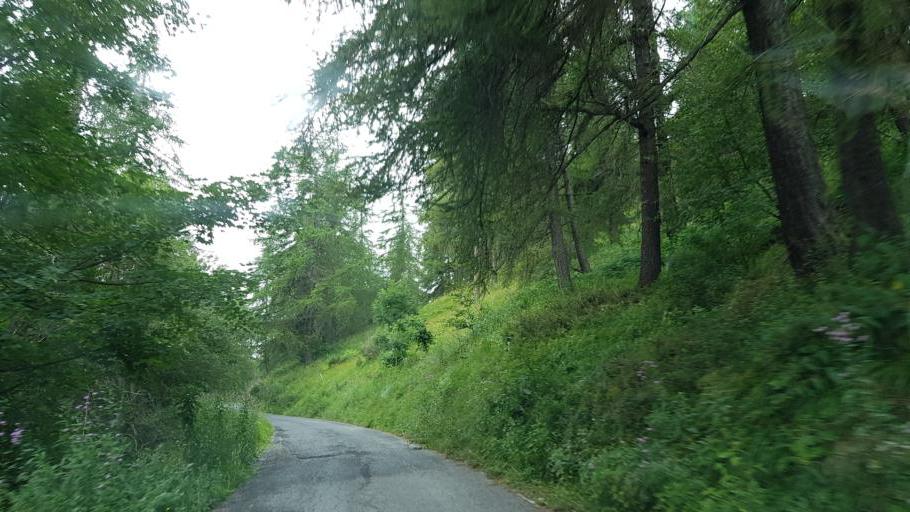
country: IT
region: Piedmont
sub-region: Provincia di Cuneo
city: Stroppo
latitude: 44.5179
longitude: 7.1084
